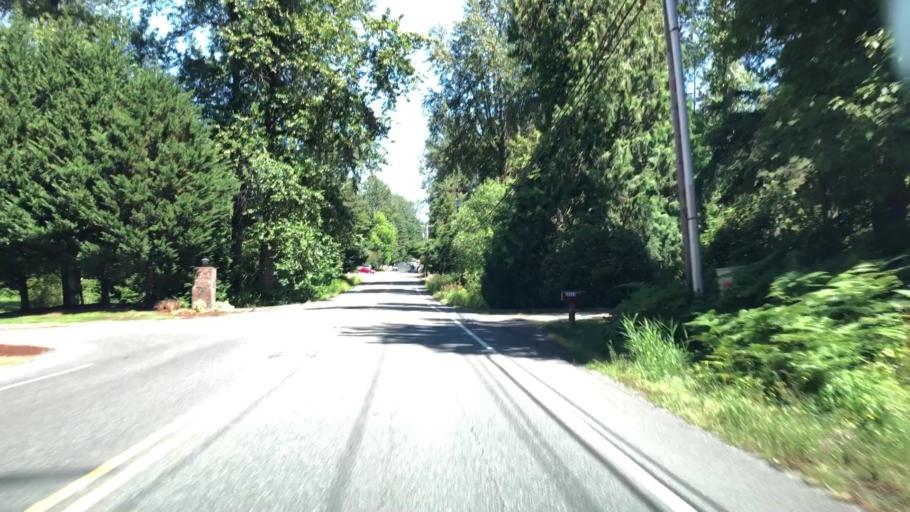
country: US
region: Washington
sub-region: King County
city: Cottage Lake
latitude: 47.7185
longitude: -122.0699
